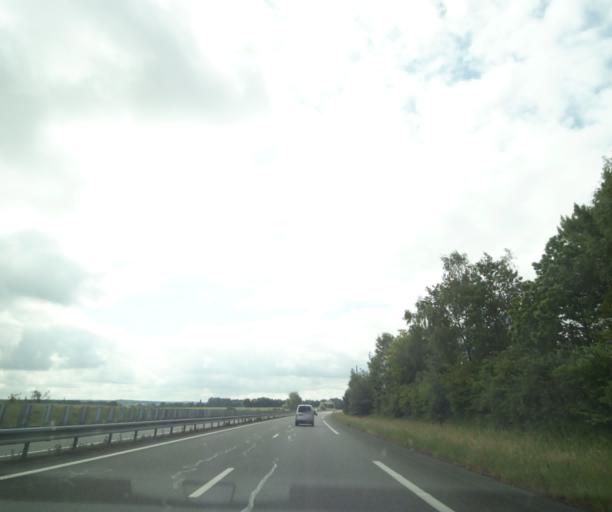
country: FR
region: Pays de la Loire
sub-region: Departement de Maine-et-Loire
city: Baune
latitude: 47.5323
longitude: -0.3191
